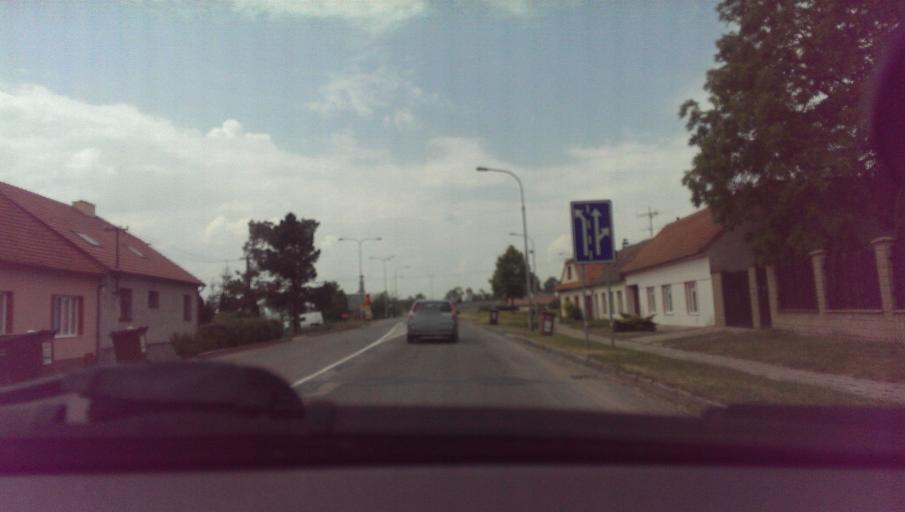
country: CZ
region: South Moravian
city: Slavkov u Brna
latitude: 49.1520
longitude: 16.8682
